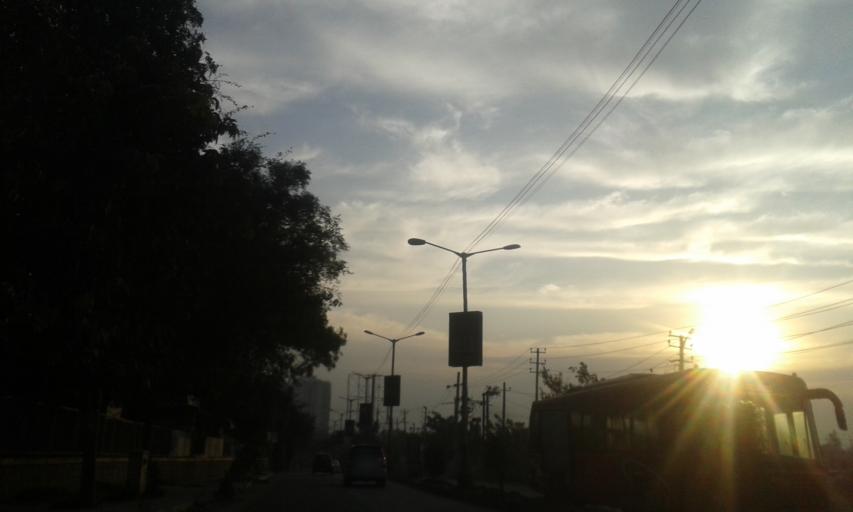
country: IN
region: Karnataka
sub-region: Bangalore Rural
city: Hoskote
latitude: 12.9919
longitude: 77.7565
